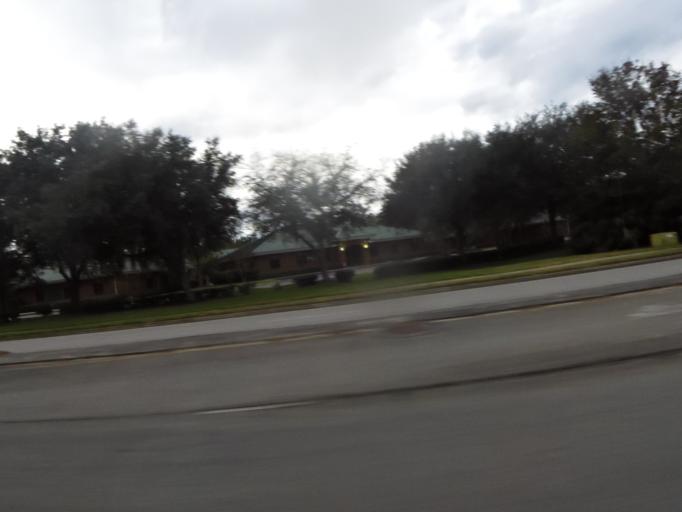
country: US
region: Florida
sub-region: Duval County
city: Jacksonville
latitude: 30.2453
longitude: -81.5830
